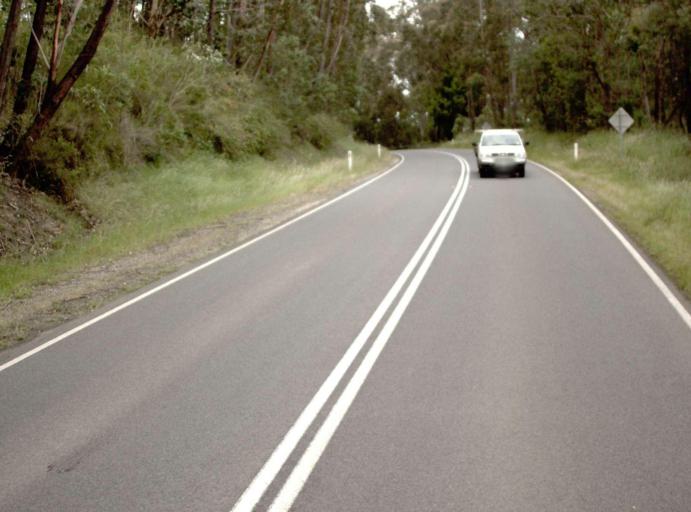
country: AU
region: Victoria
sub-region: Baw Baw
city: Warragul
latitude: -38.0537
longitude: 145.9667
